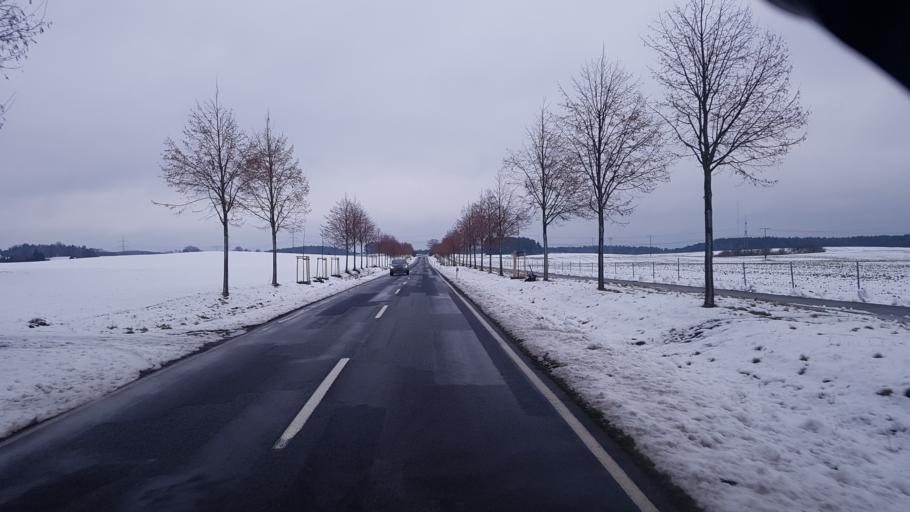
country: DE
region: Brandenburg
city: Lawitz
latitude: 52.0876
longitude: 14.5568
